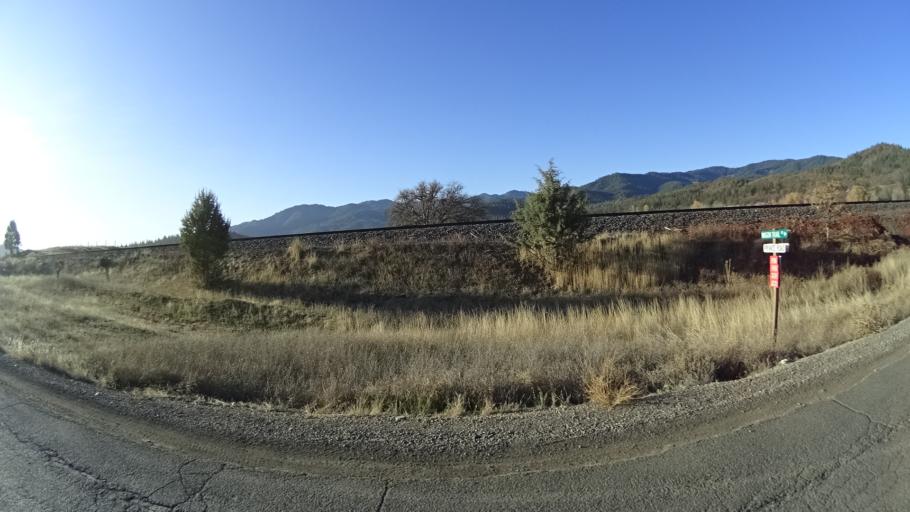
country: US
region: Oregon
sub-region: Jackson County
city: Ashland
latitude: 42.0007
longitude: -122.6369
